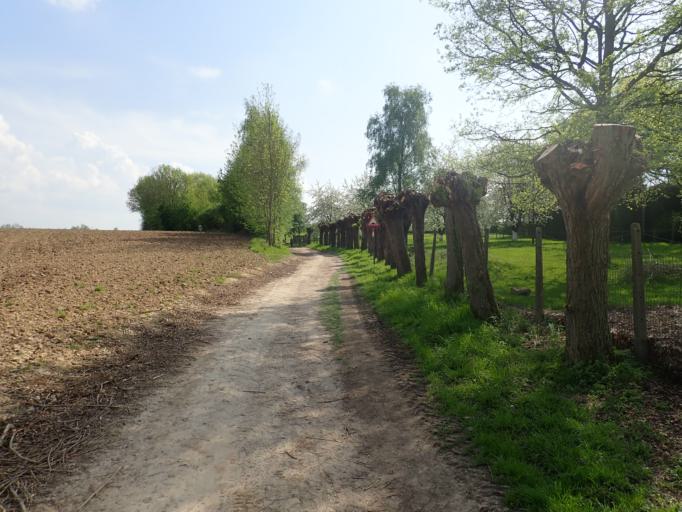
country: BE
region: Flanders
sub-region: Provincie Vlaams-Brabant
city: Merchtem
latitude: 50.9168
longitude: 4.2601
